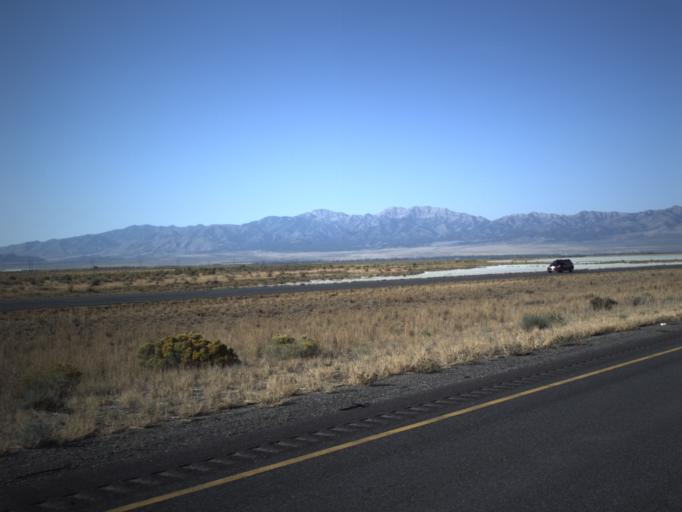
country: US
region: Utah
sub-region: Tooele County
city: Stansbury park
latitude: 40.6628
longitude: -112.3329
